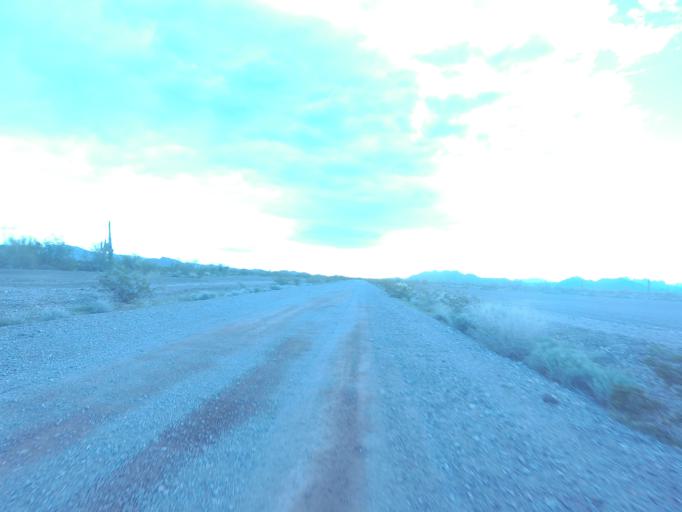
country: US
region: Arizona
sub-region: La Paz County
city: Quartzsite
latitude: 33.5346
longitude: -114.2012
